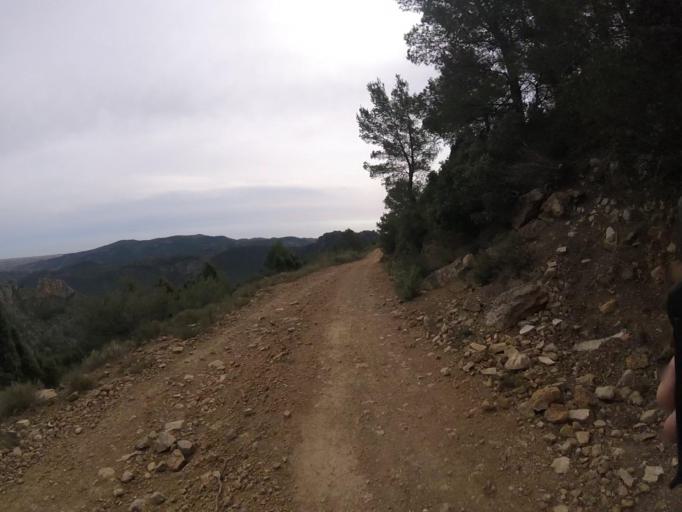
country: ES
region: Valencia
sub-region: Provincia de Castello
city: Benicassim
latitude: 40.0871
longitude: 0.0392
